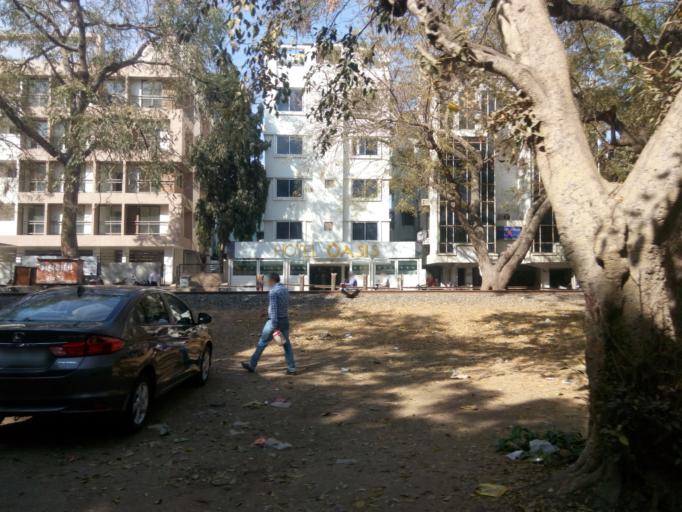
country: IN
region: Gujarat
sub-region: Ahmadabad
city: Ahmedabad
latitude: 23.0394
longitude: 72.5668
